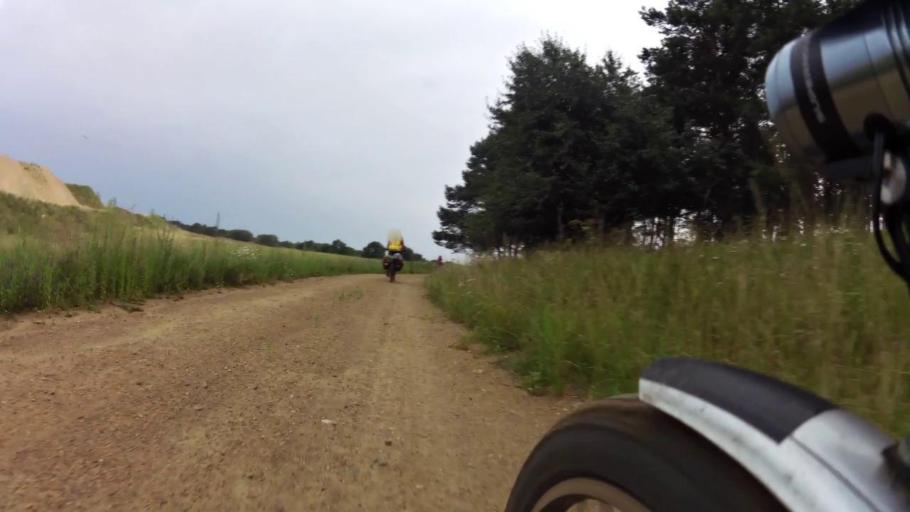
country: PL
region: West Pomeranian Voivodeship
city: Trzcinsko Zdroj
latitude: 52.8755
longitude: 14.6032
